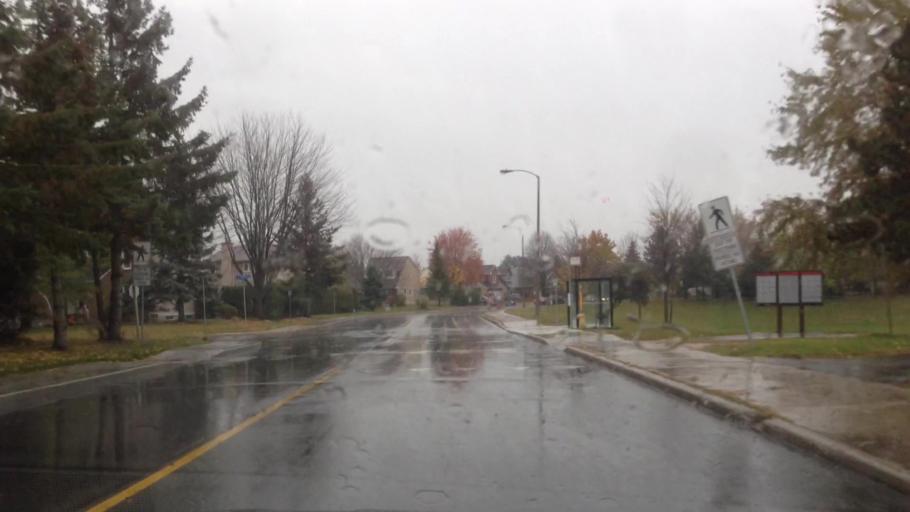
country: CA
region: Ontario
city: Clarence-Rockland
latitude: 45.4656
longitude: -75.4804
